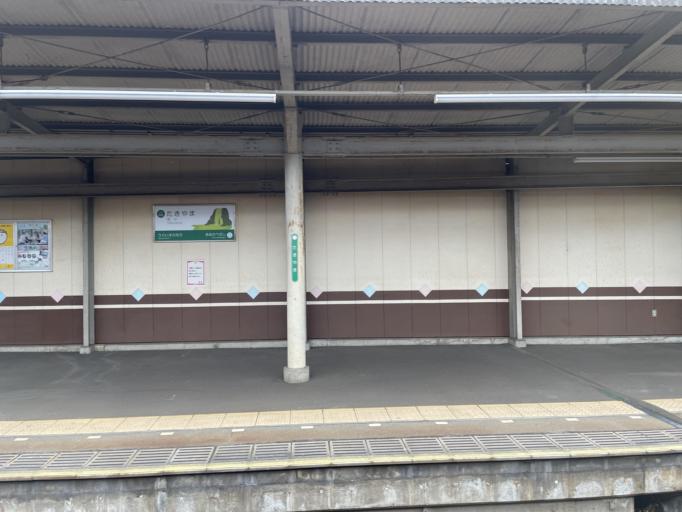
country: JP
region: Osaka
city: Ikeda
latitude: 34.8429
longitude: 135.4213
